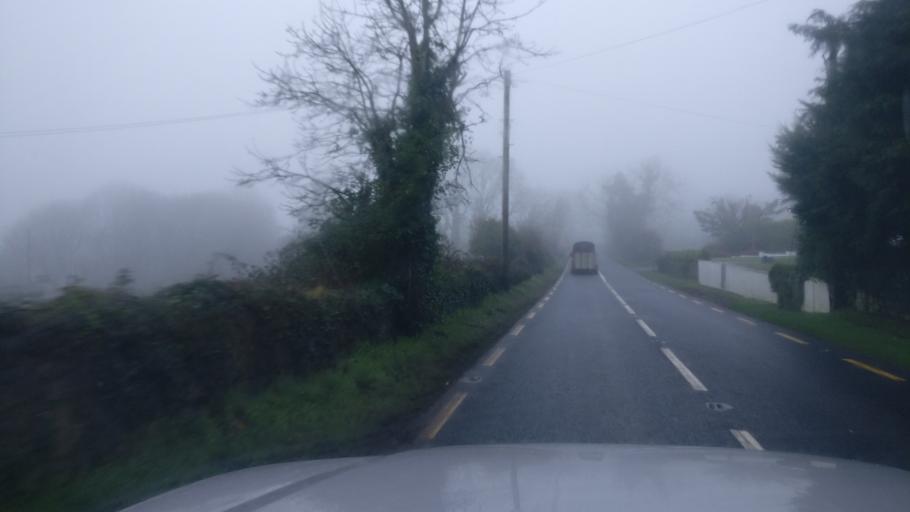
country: IE
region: Connaught
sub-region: County Galway
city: Loughrea
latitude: 53.1576
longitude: -8.6876
